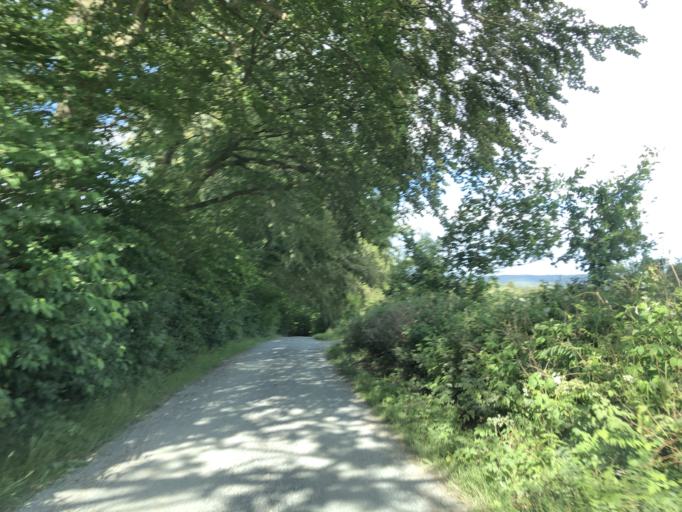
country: DK
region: South Denmark
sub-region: Vejle Kommune
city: Brejning
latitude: 55.6766
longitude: 9.6571
